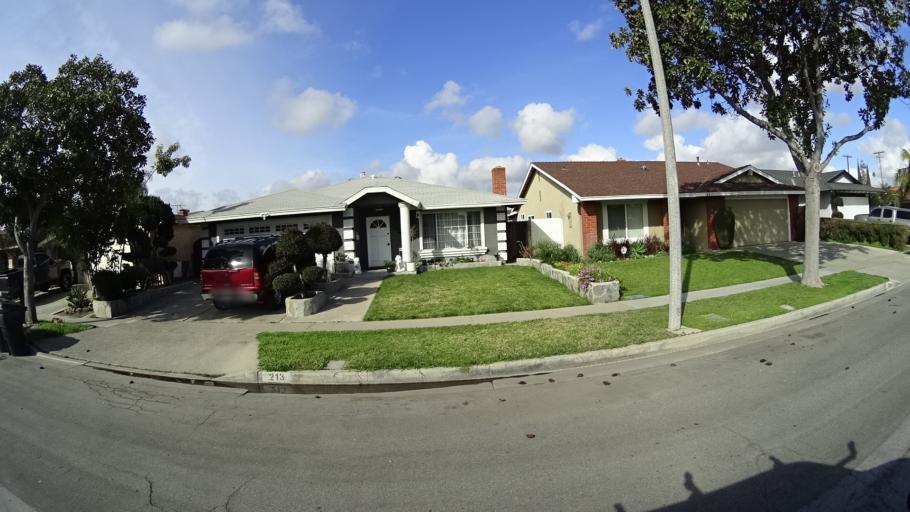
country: US
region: California
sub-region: Orange County
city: Stanton
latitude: 33.8298
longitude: -117.9734
